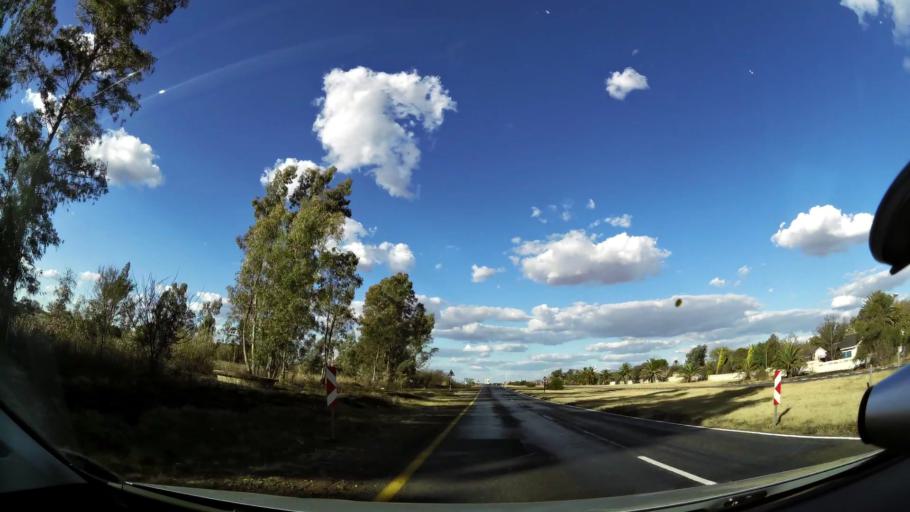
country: ZA
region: North-West
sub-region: Dr Kenneth Kaunda District Municipality
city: Stilfontein
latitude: -26.8410
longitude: 26.7544
